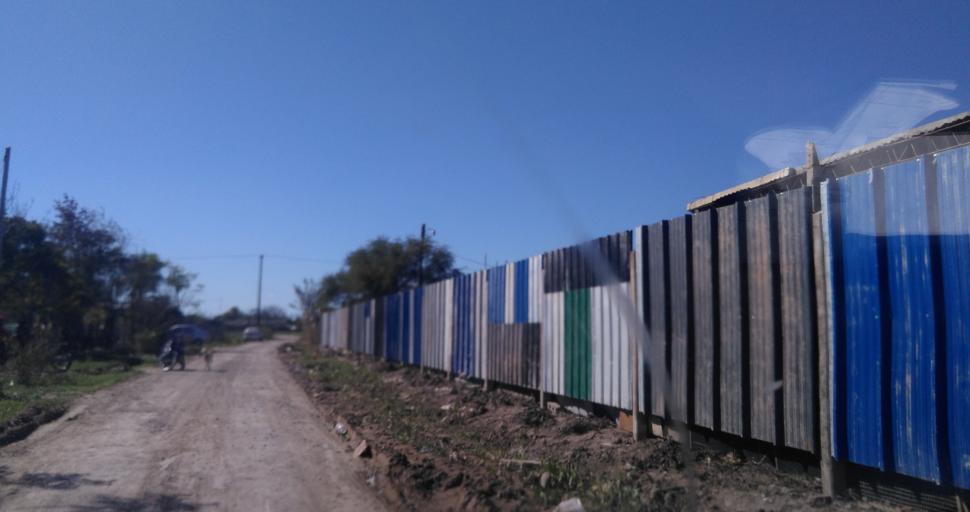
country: AR
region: Chaco
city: Fontana
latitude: -27.4312
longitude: -59.0213
